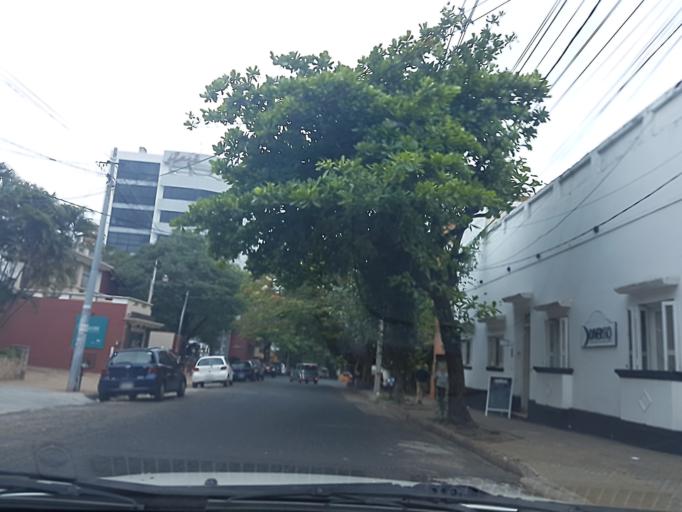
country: PY
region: Asuncion
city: Asuncion
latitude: -25.2858
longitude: -57.6141
